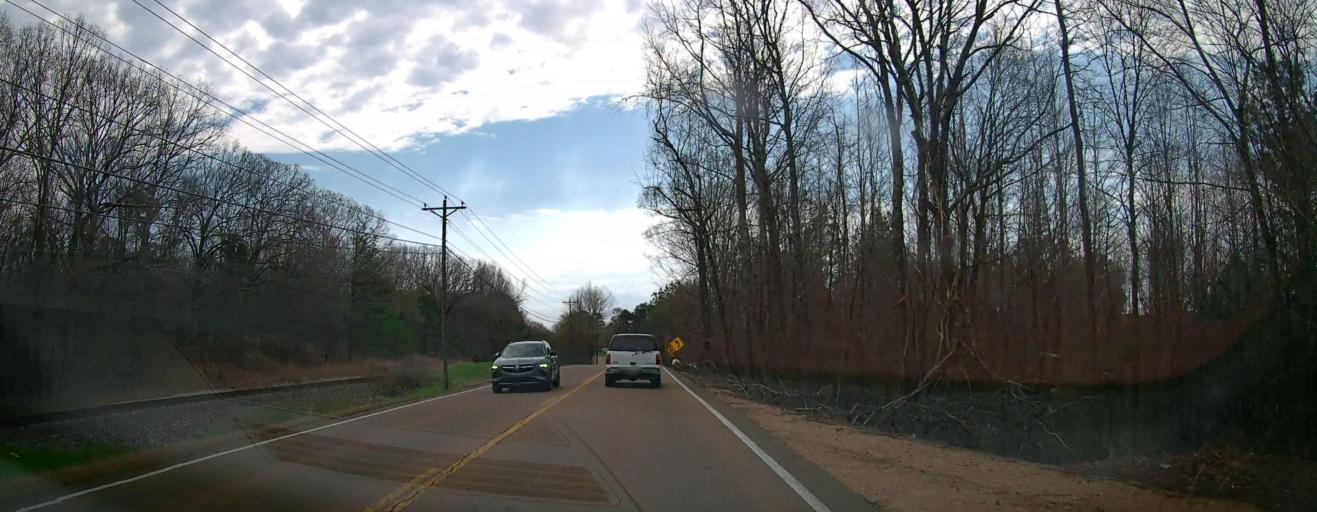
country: US
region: Mississippi
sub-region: Marshall County
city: Byhalia
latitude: 34.8910
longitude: -89.7329
